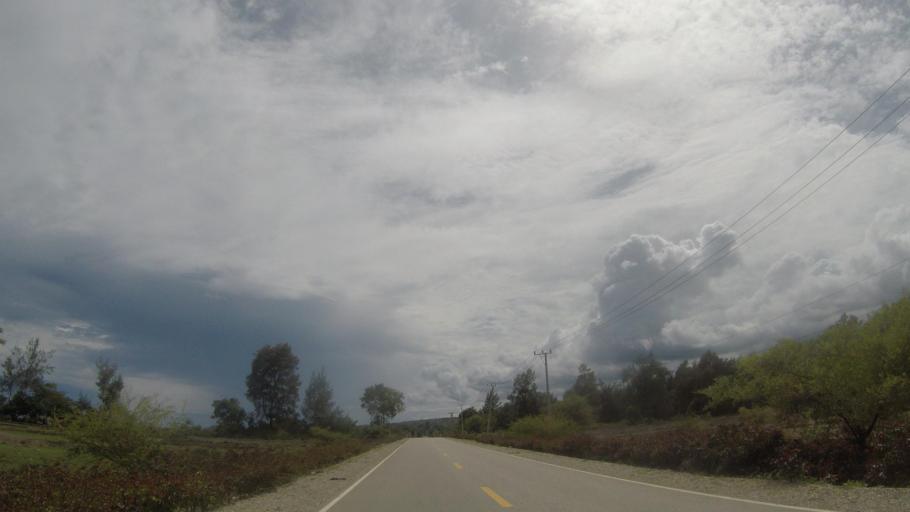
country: TL
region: Baucau
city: Baucau
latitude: -8.4796
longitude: 126.5798
